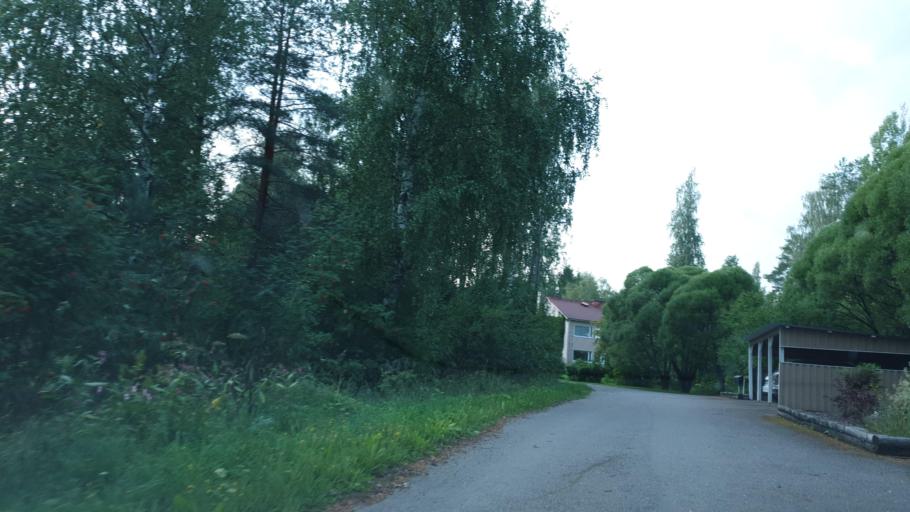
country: FI
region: Northern Savo
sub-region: Varkaus
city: Leppaevirta
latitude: 62.5870
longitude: 27.6104
